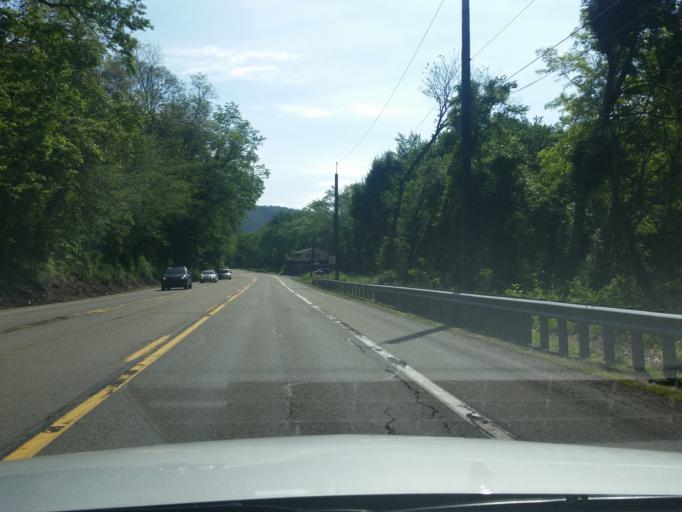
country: US
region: Pennsylvania
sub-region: Luzerne County
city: Nanticoke
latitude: 41.2160
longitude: -76.0372
